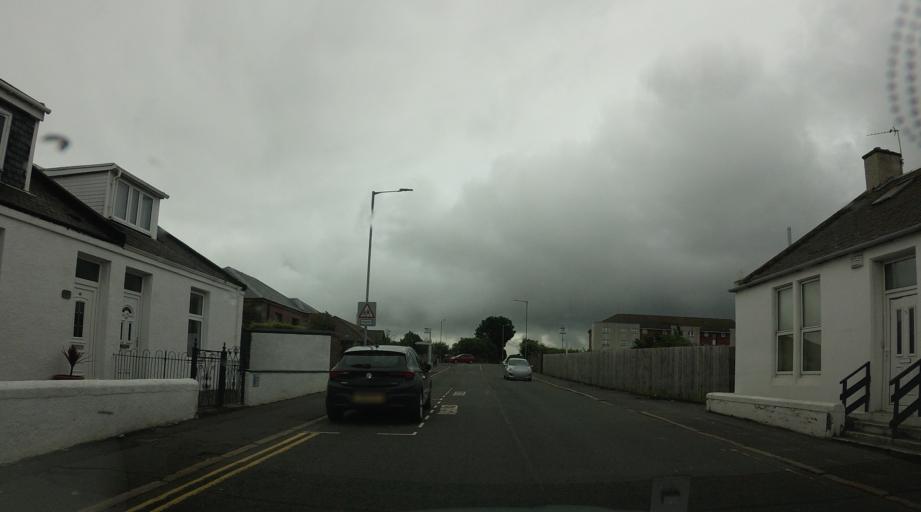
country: GB
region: Scotland
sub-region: South Ayrshire
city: Prestwick
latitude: 55.4721
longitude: -4.6187
